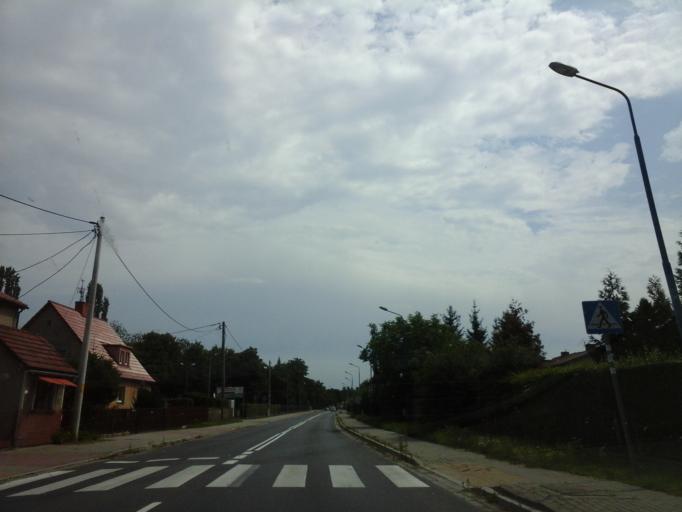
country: PL
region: Lower Silesian Voivodeship
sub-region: Powiat strzelinski
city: Strzelin
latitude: 50.7890
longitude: 17.0671
